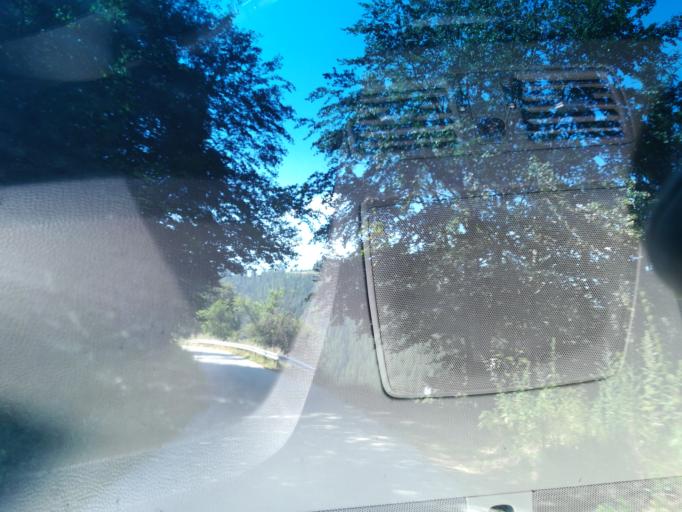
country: BG
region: Smolyan
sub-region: Obshtina Smolyan
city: Smolyan
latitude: 41.6587
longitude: 24.8278
